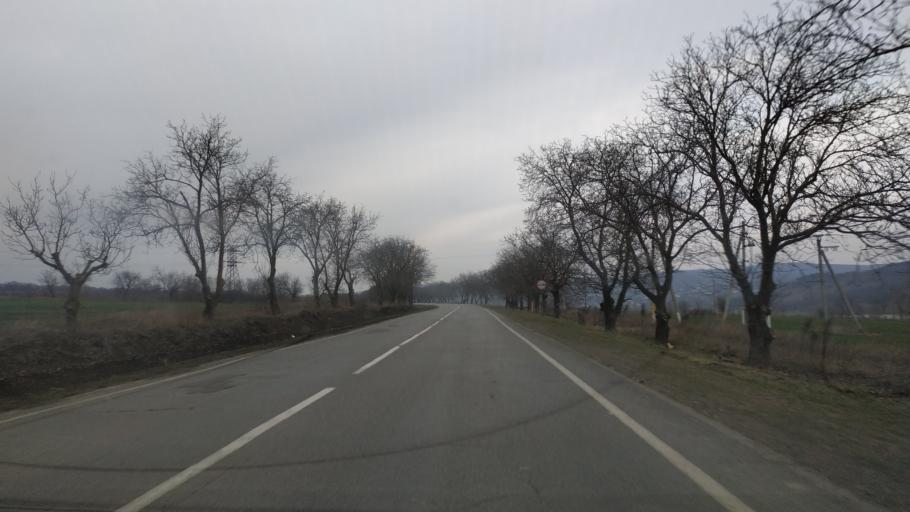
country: MD
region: Hincesti
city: Hincesti
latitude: 46.7792
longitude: 28.5247
